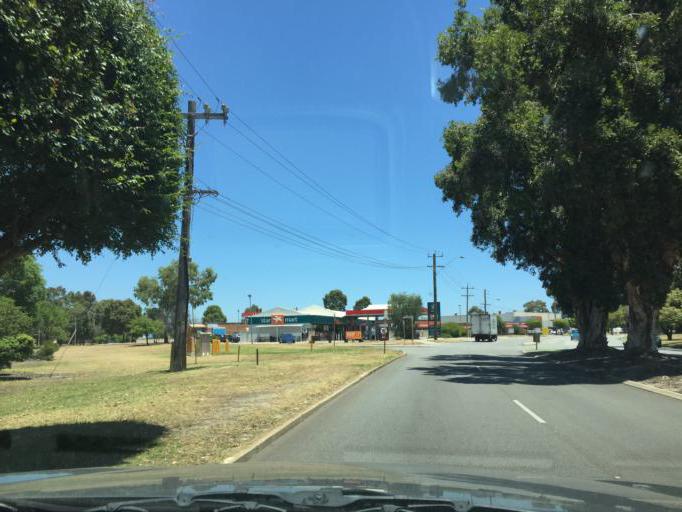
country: AU
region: Western Australia
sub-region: Canning
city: Canning Vale
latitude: -32.0628
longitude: 115.9274
